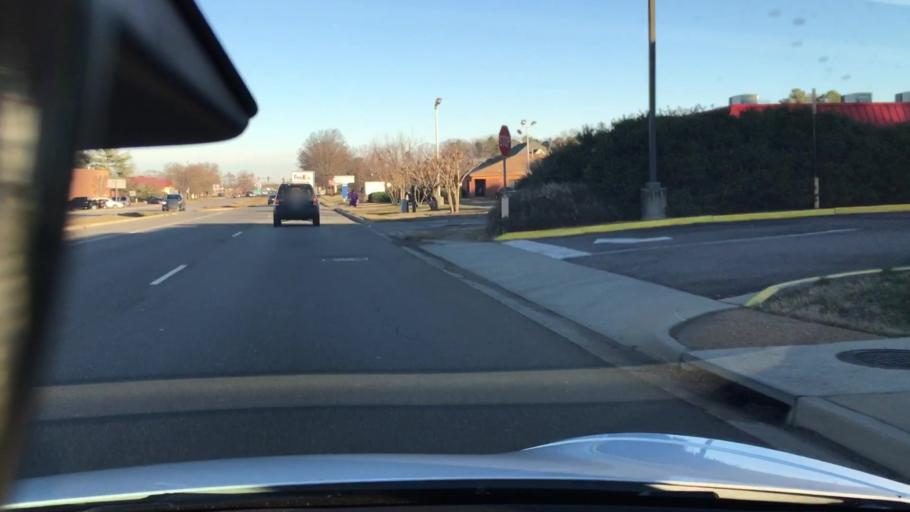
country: US
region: Virginia
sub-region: Henrico County
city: Fort Lee
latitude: 37.5185
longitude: -77.3504
